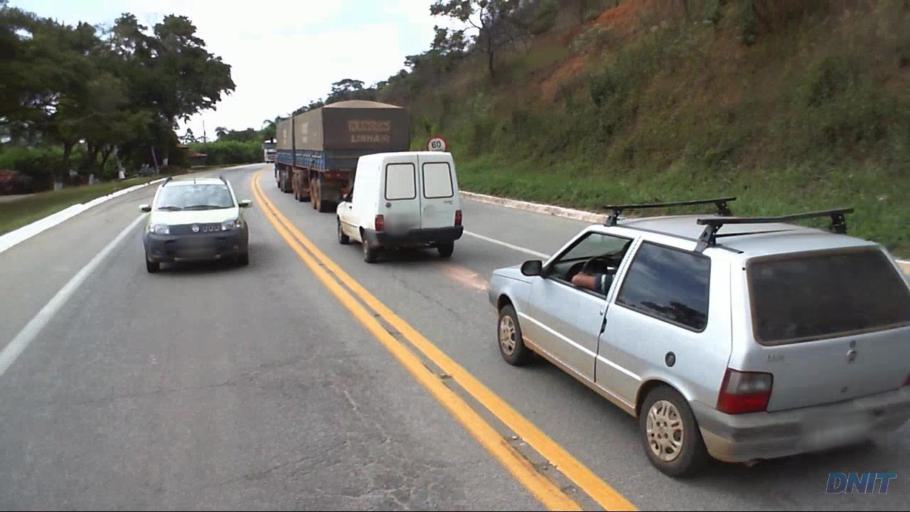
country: BR
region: Minas Gerais
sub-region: Caete
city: Caete
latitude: -19.7666
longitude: -43.6446
